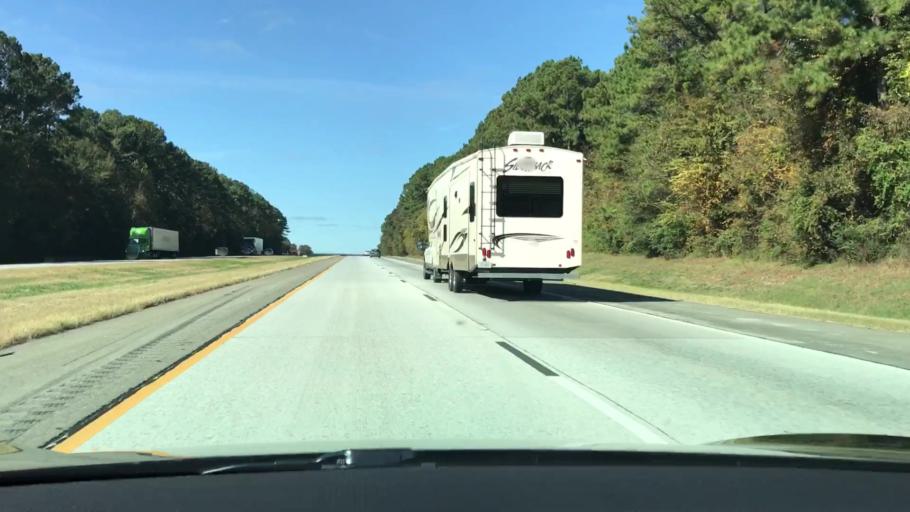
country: US
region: Georgia
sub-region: Putnam County
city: Jefferson
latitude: 33.5376
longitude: -83.3071
